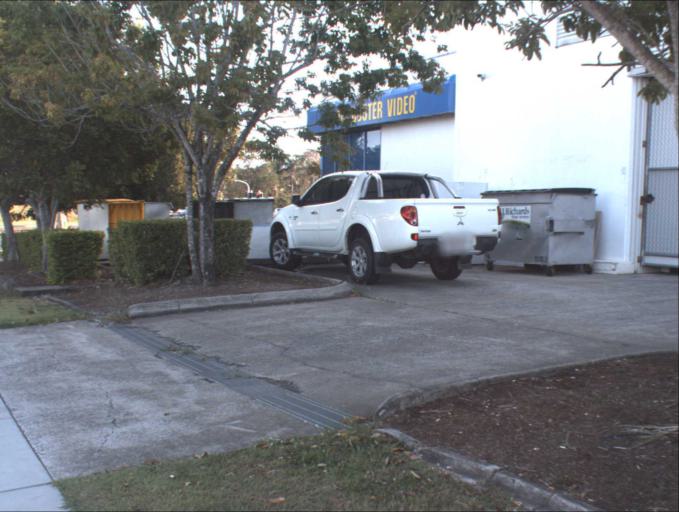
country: AU
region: Queensland
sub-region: Logan
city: Beenleigh
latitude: -27.7185
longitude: 153.2041
